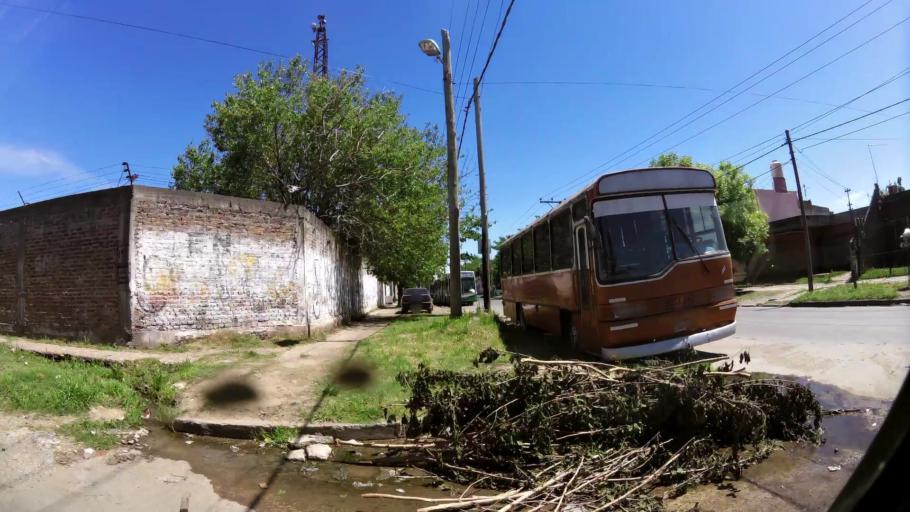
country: AR
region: Buenos Aires
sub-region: Partido de Lanus
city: Lanus
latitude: -34.7384
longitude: -58.3459
